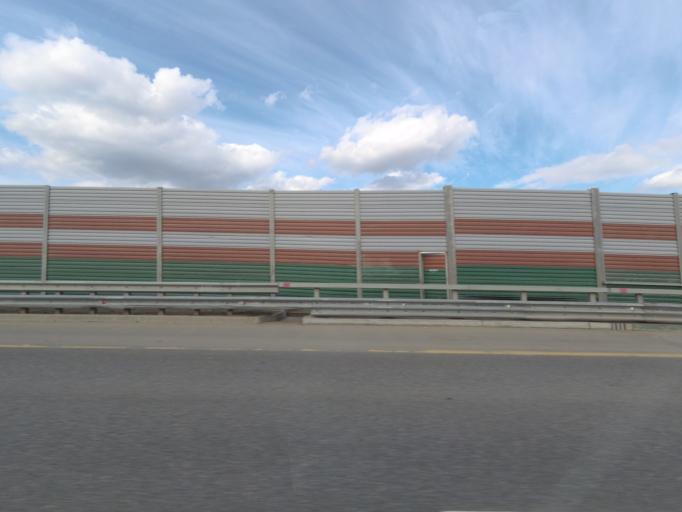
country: RU
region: Moskovskaya
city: Levoberezhnaya
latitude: 55.9026
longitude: 37.4845
